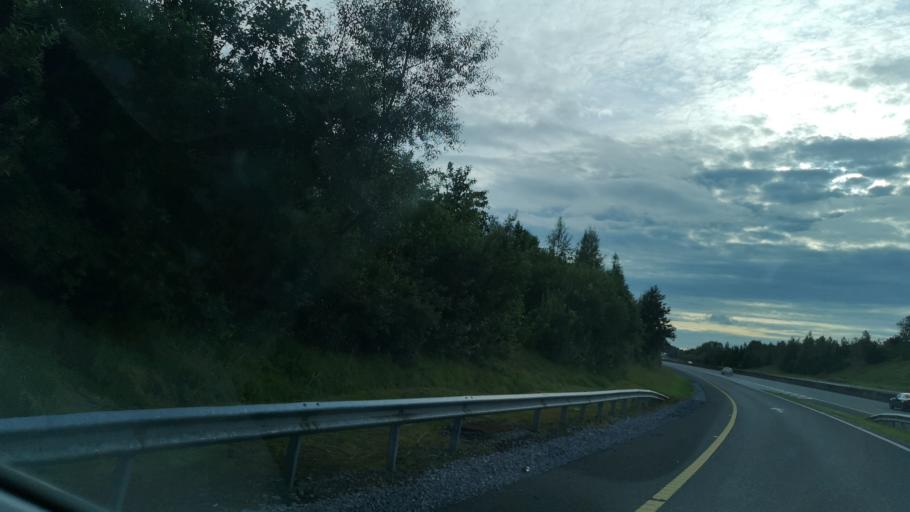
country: IE
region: Connaught
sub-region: County Galway
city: Ballinasloe
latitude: 53.3148
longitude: -8.2469
